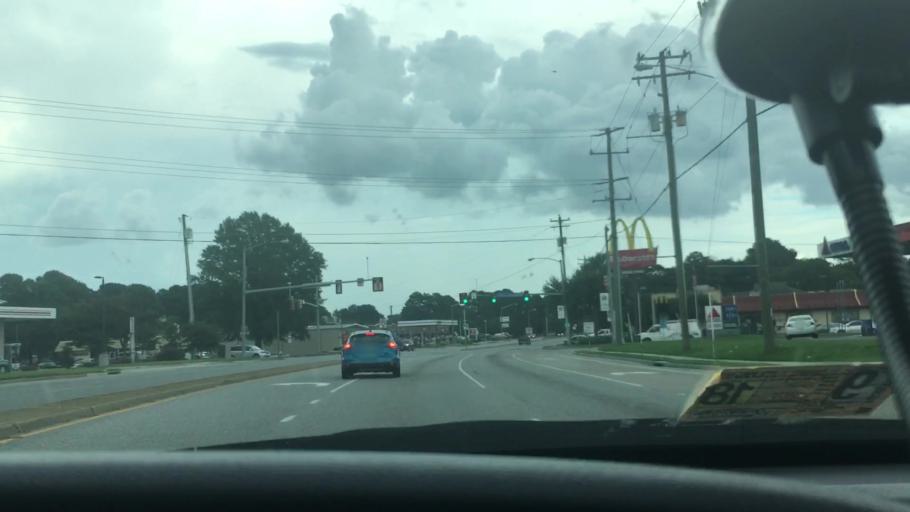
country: US
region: Virginia
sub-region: City of Portsmouth
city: Portsmouth Heights
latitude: 36.8249
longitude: -76.4060
